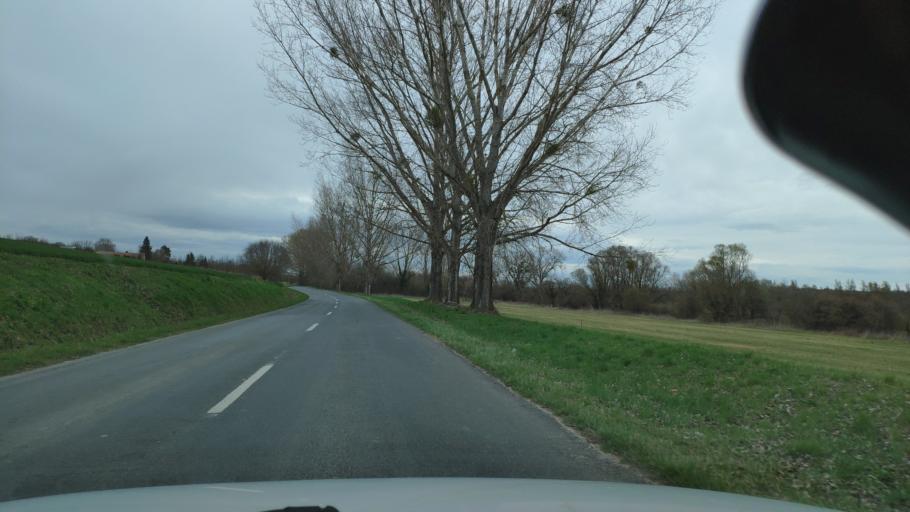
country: HU
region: Zala
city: Sarmellek
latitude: 46.6695
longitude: 17.1125
